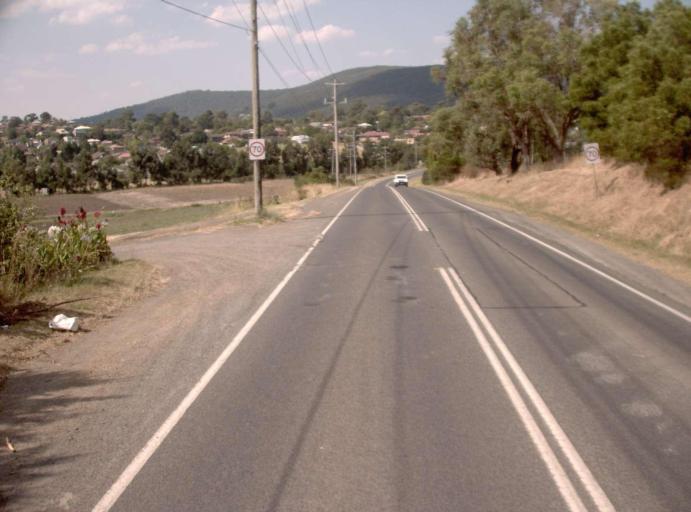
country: AU
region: Victoria
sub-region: Knox
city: Ferntree Gully
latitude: -37.9038
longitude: 145.2833
